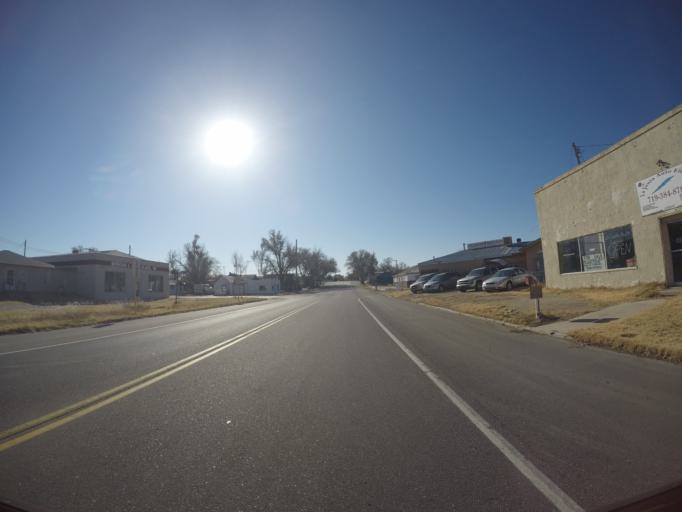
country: US
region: Colorado
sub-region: Otero County
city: La Junta
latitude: 37.9875
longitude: -103.5333
